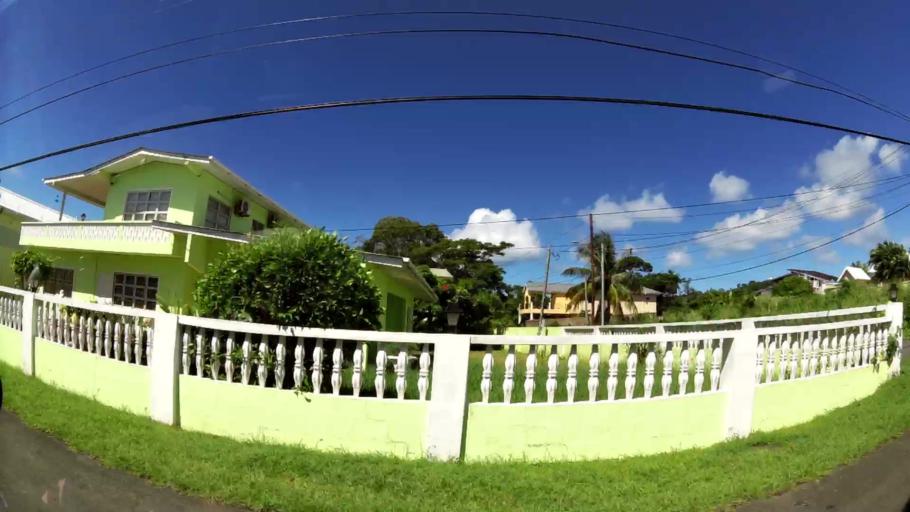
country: TT
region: Tobago
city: Scarborough
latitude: 11.1675
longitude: -60.7632
